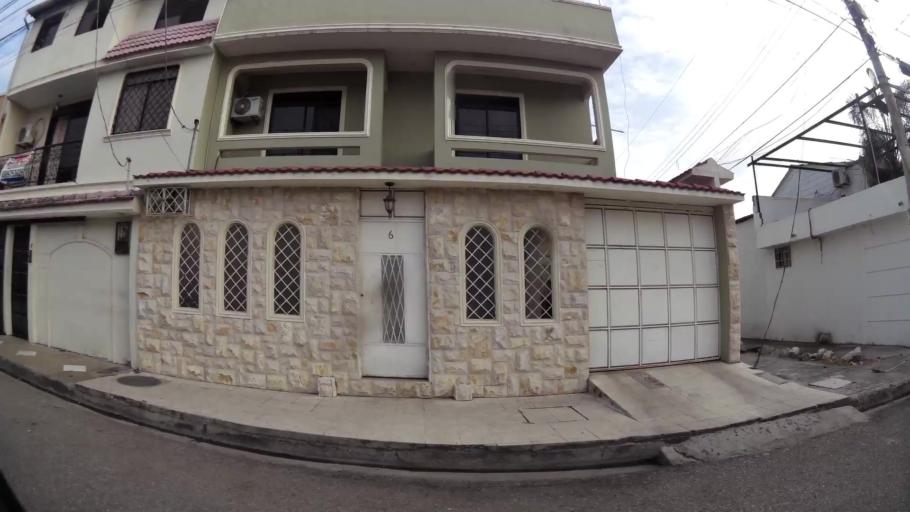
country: EC
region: Guayas
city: Eloy Alfaro
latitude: -2.1339
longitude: -79.8933
